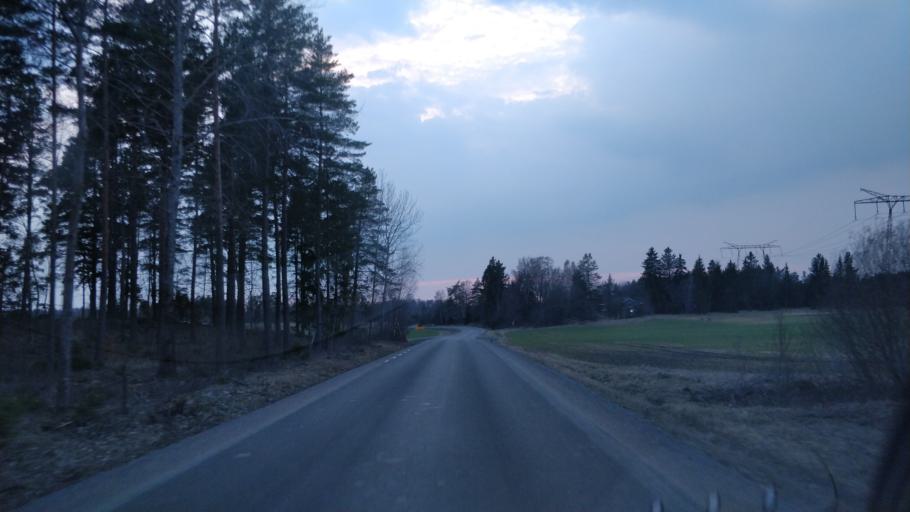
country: SE
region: Uppsala
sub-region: Enkopings Kommun
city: Orsundsbro
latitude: 59.7247
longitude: 17.2790
